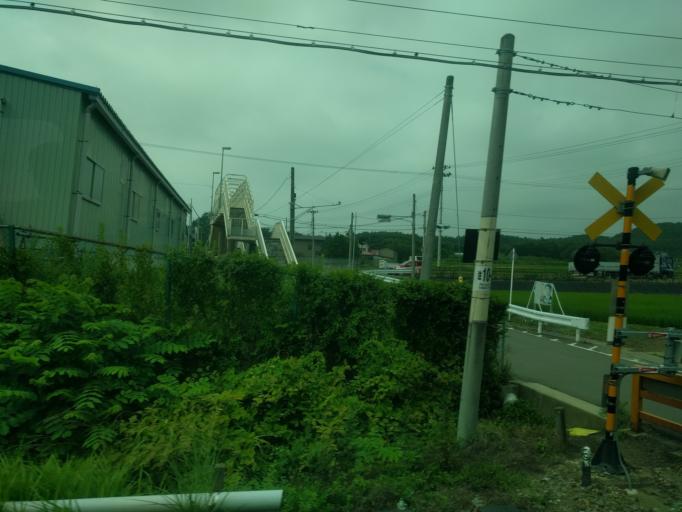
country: JP
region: Fukushima
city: Motomiya
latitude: 37.4725
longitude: 140.3086
